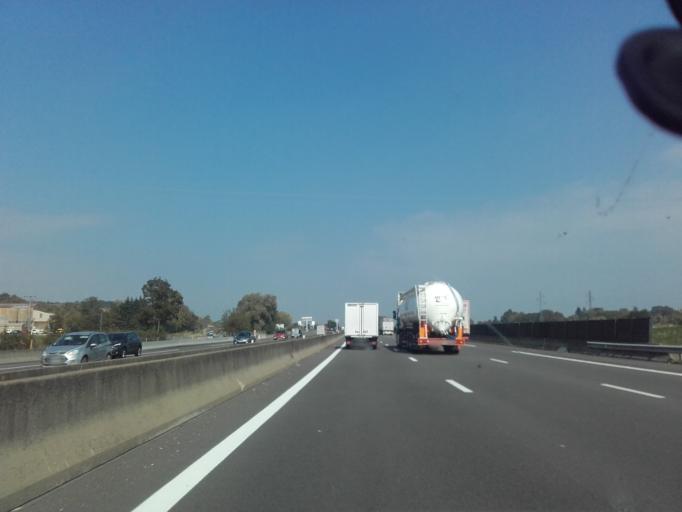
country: FR
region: Bourgogne
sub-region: Departement de Saone-et-Loire
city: Saint-Martin-Belle-Roche
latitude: 46.3779
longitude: 4.8452
